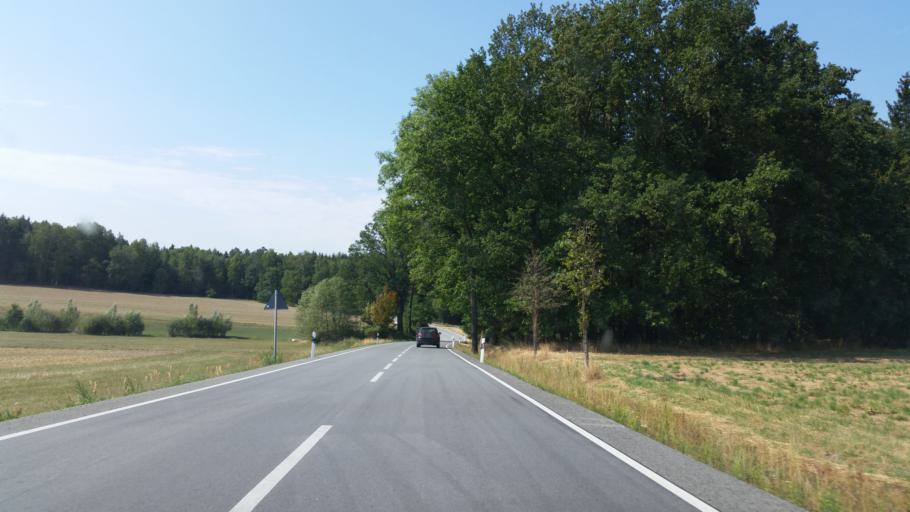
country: DE
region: Saxony
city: Grosshennersdorf
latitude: 50.9810
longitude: 14.7591
